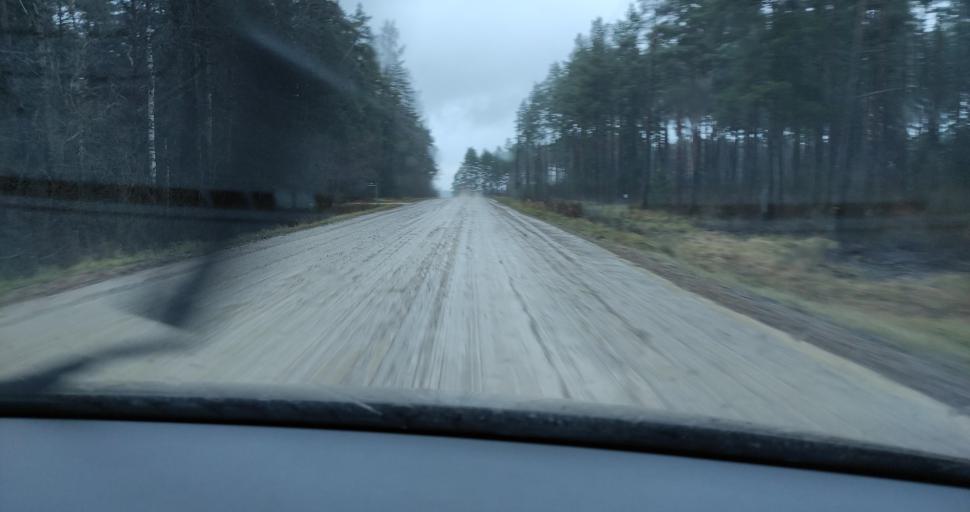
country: LV
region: Skrunda
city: Skrunda
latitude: 56.6856
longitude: 22.2220
